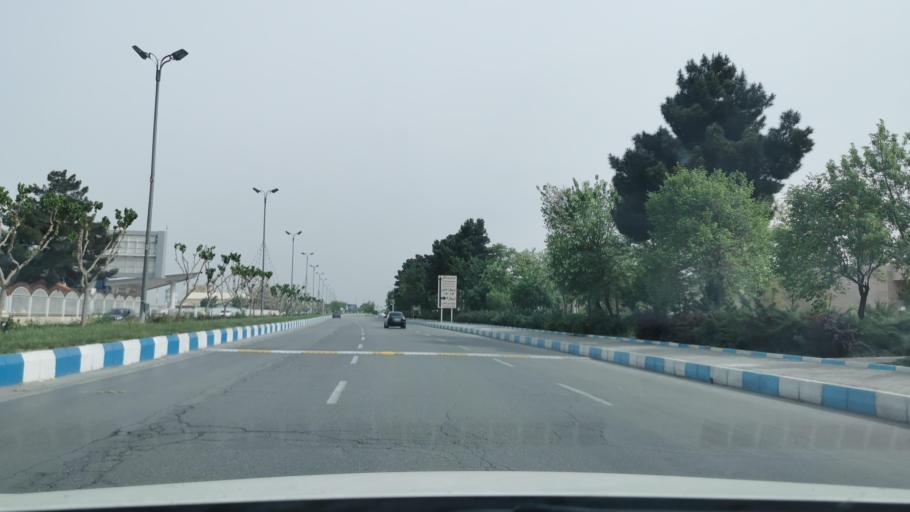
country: IR
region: Razavi Khorasan
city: Mashhad
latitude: 36.2347
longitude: 59.6320
